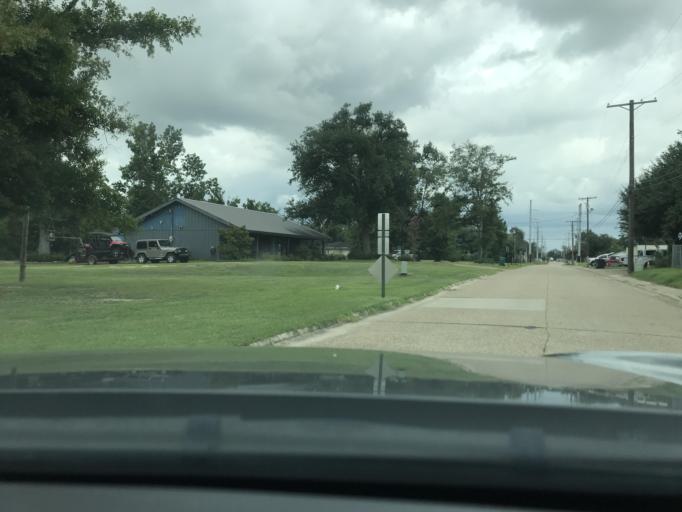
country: US
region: Louisiana
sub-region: Calcasieu Parish
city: Westlake
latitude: 30.2442
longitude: -93.2538
